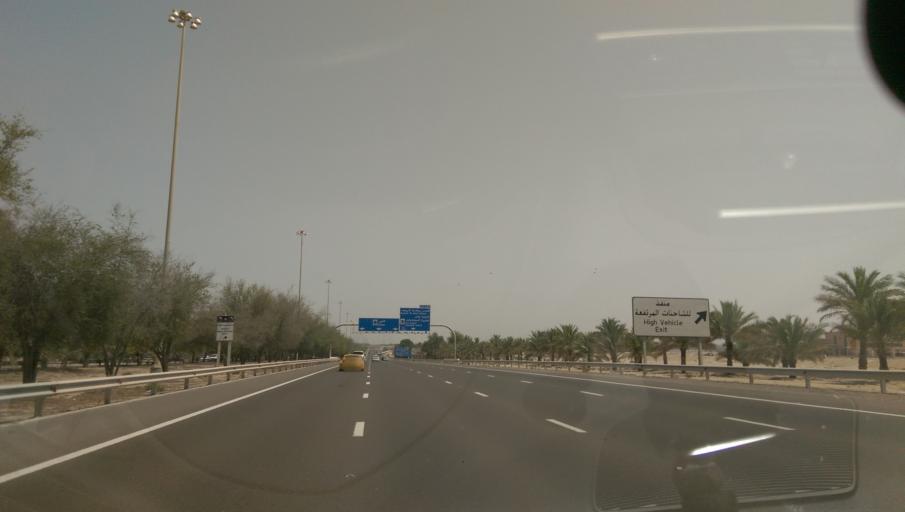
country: AE
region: Abu Dhabi
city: Abu Dhabi
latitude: 24.4539
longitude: 54.6787
